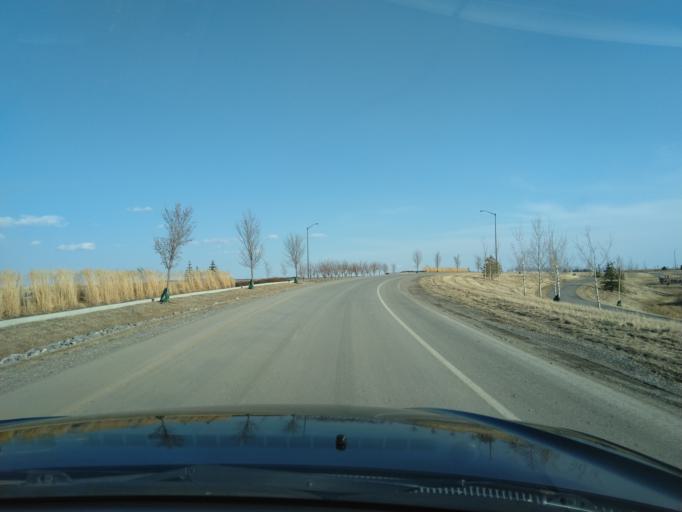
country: CA
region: Alberta
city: Cochrane
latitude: 51.1118
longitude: -114.3915
